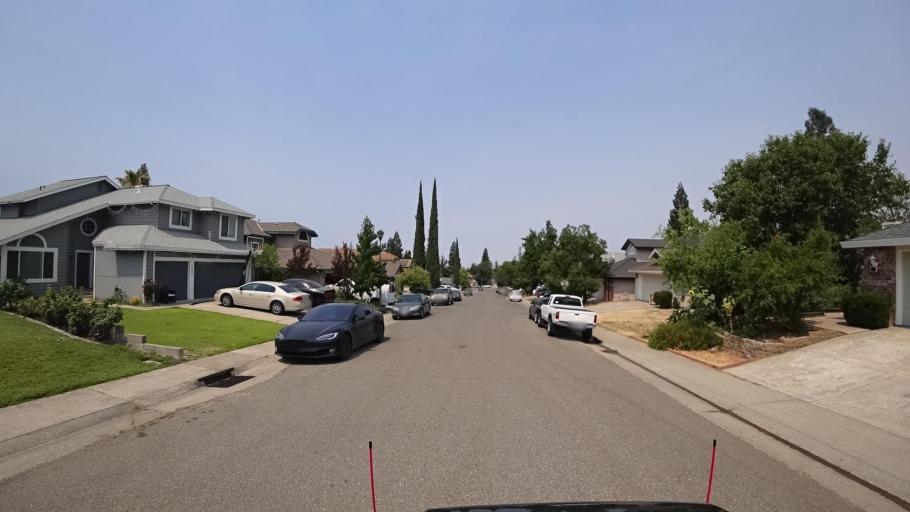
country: US
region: California
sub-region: Placer County
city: Rocklin
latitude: 38.8036
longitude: -121.2574
